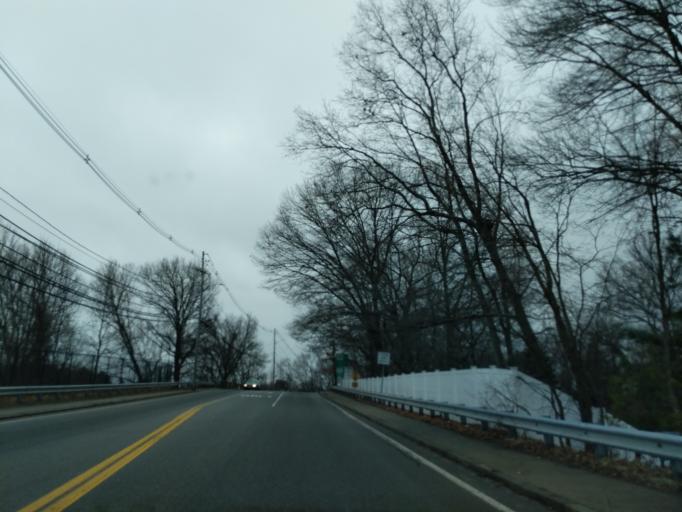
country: US
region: Massachusetts
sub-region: Middlesex County
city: Natick
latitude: 42.2846
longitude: -71.3754
